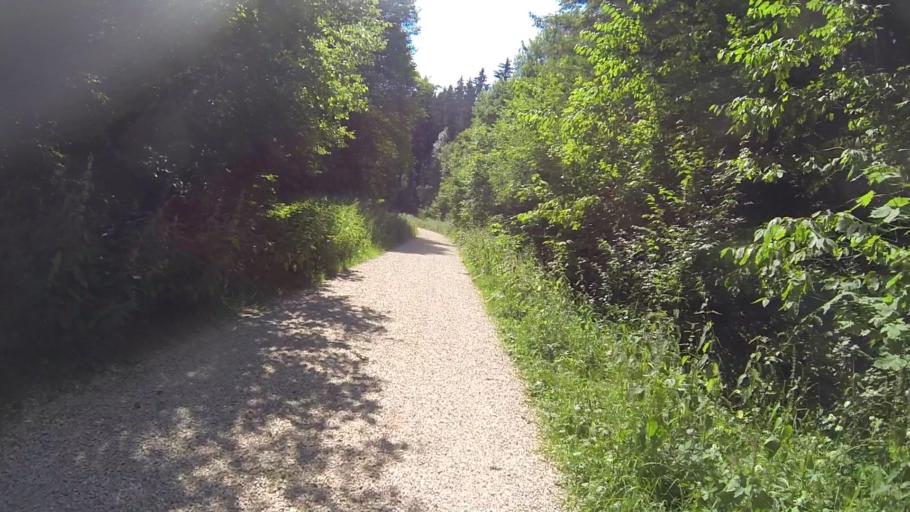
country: DE
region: Baden-Wuerttemberg
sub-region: Regierungsbezirk Stuttgart
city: Heidenheim an der Brenz
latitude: 48.6651
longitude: 10.1831
